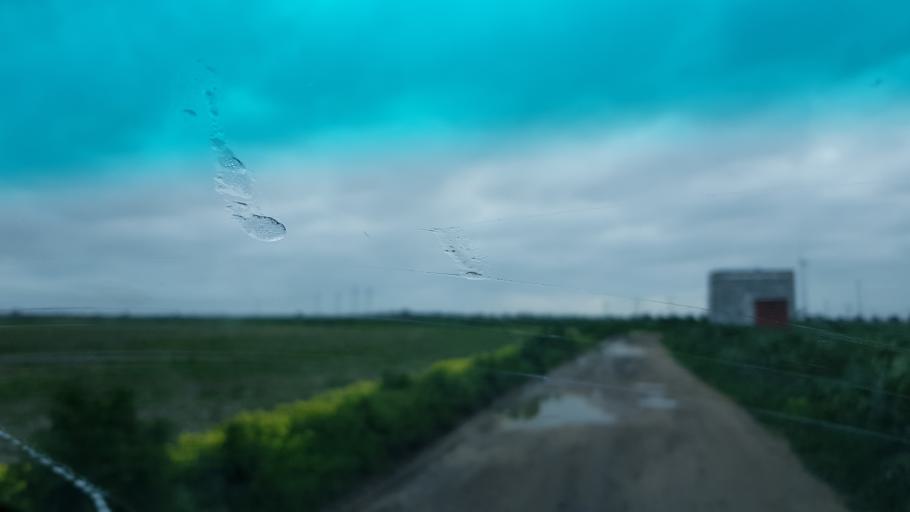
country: IT
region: Apulia
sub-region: Provincia di Brindisi
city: Tuturano
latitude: 40.5684
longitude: 17.9939
